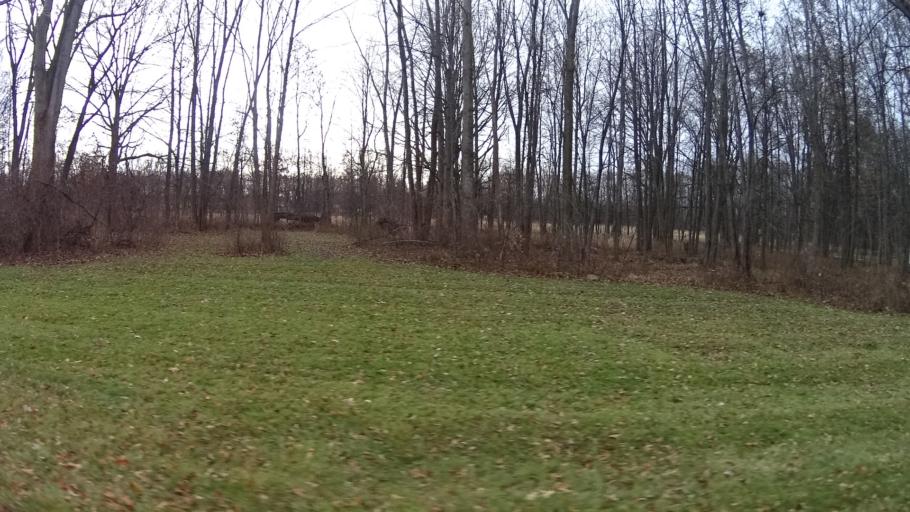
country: US
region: Ohio
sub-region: Lorain County
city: North Ridgeville
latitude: 41.3732
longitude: -82.0273
